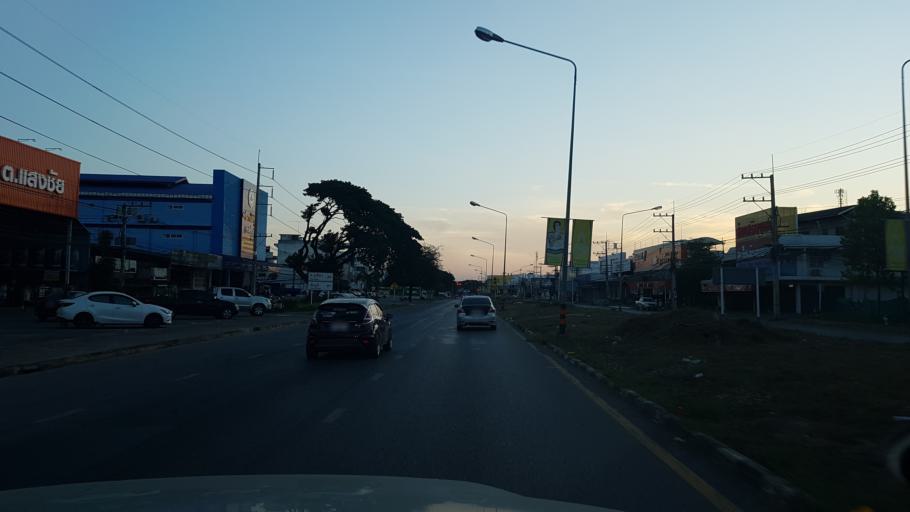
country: TH
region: Khon Kaen
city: Chum Phae
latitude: 16.5395
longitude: 102.1077
